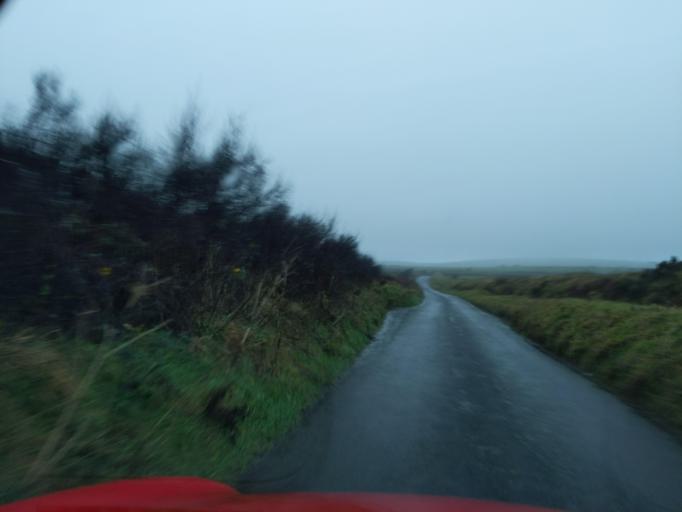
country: GB
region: England
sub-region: Cornwall
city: Camelford
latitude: 50.6552
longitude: -4.7018
